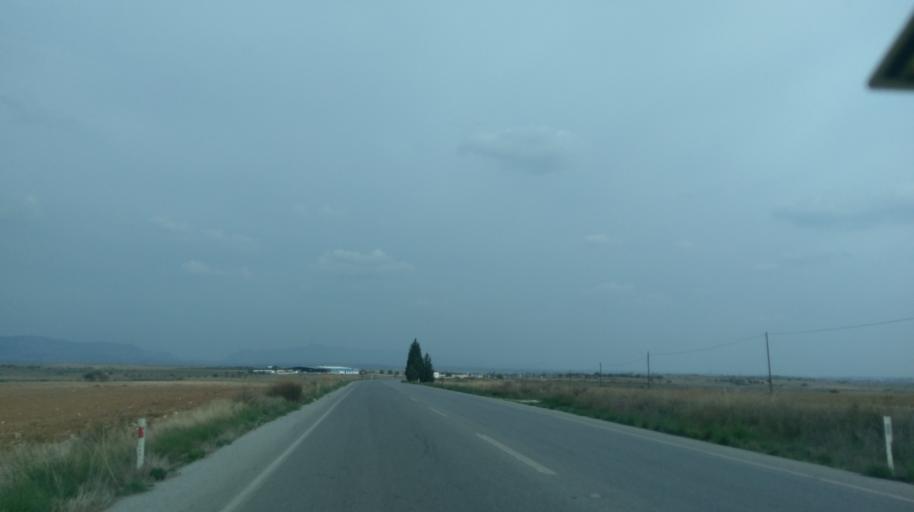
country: CY
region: Ammochostos
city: Lefkonoiko
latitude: 35.2536
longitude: 33.6323
